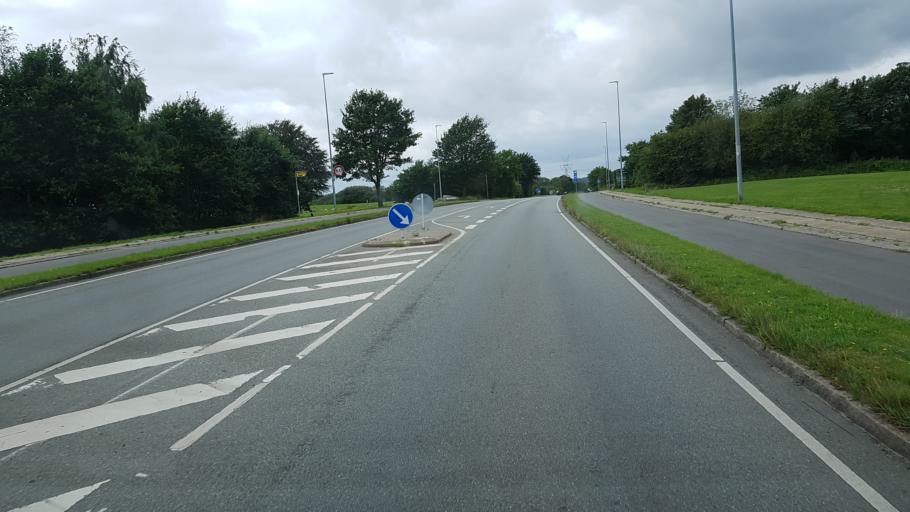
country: DK
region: South Denmark
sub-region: Kolding Kommune
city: Kolding
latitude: 55.4824
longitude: 9.4381
